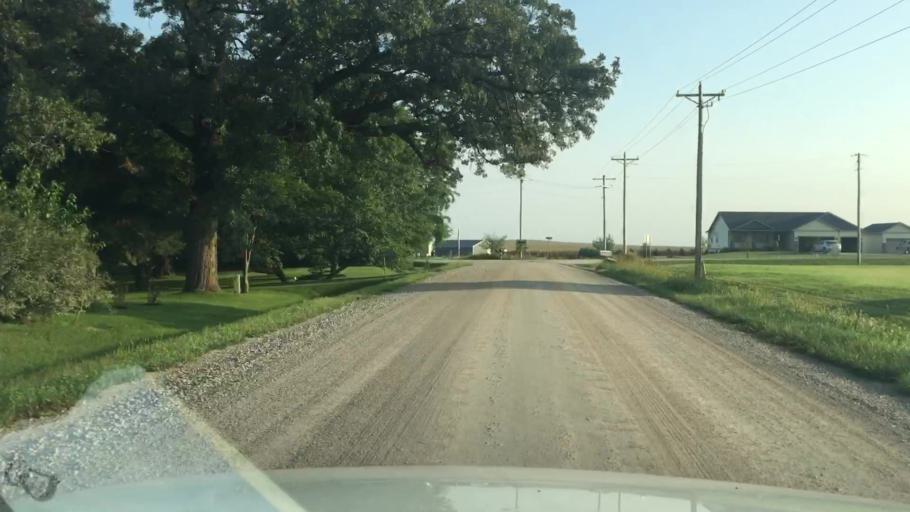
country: US
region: Iowa
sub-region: Story County
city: Huxley
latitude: 41.9168
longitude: -93.5765
